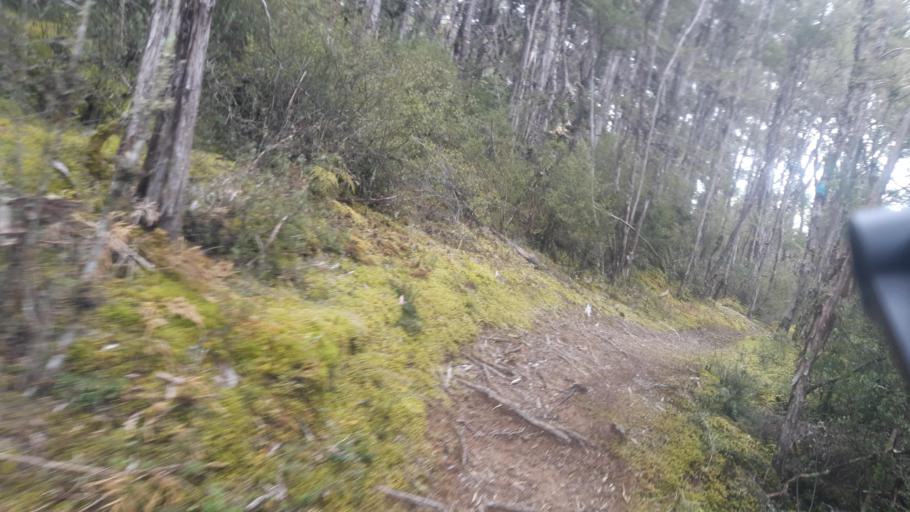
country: NZ
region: Tasman
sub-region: Tasman District
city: Wakefield
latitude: -41.7772
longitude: 172.8120
